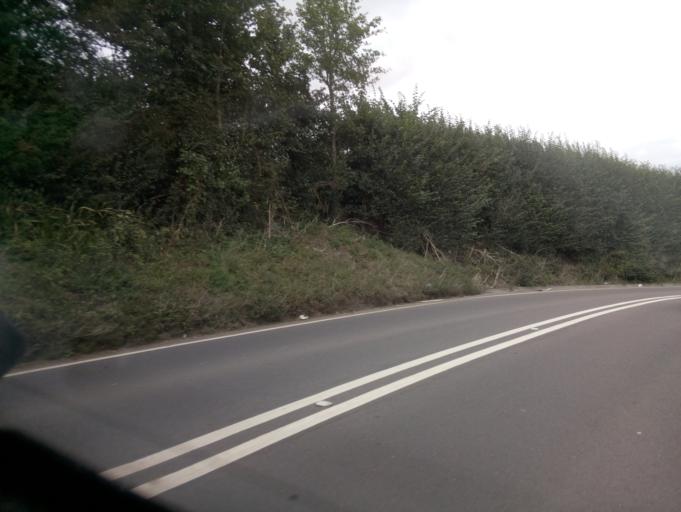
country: GB
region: England
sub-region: Devon
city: Kingsteignton
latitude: 50.5482
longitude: -3.5691
